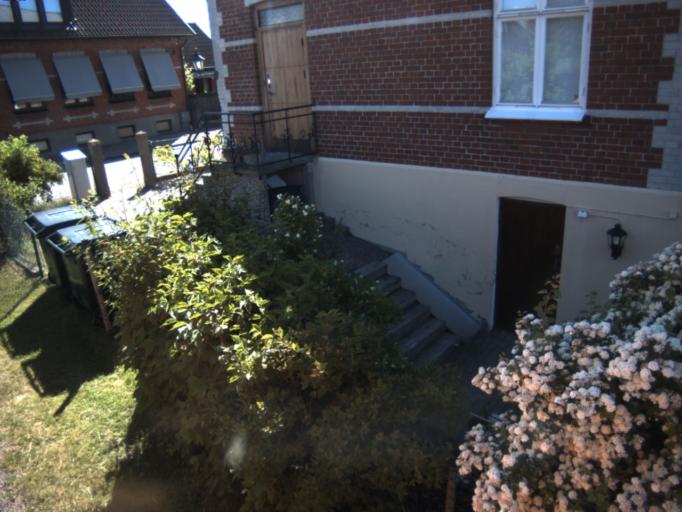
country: SE
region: Skane
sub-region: Helsingborg
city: Rydeback
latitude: 55.9934
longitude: 12.7467
